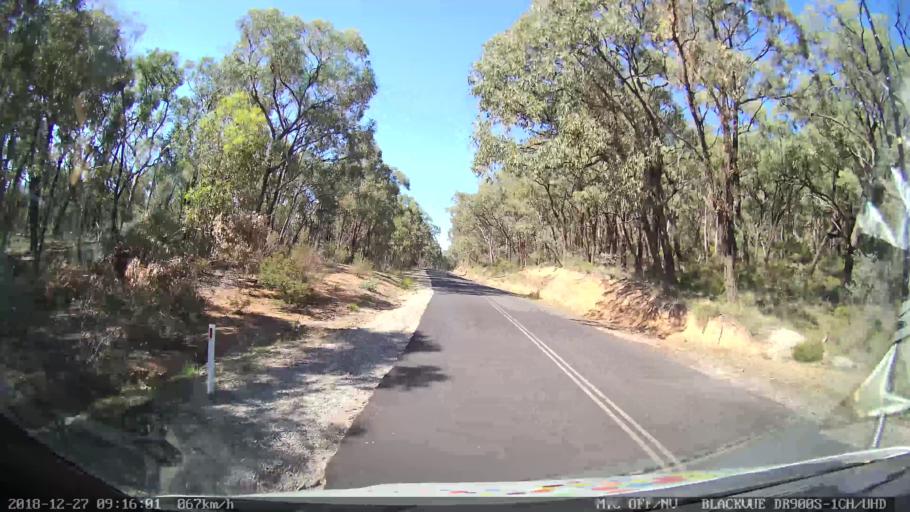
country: AU
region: New South Wales
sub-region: Lithgow
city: Portland
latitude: -33.1354
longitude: 150.0656
